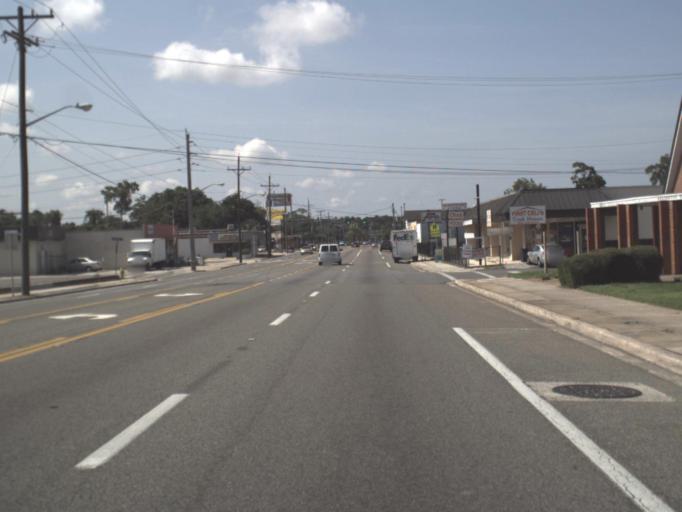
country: US
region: Florida
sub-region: Duval County
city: Jacksonville
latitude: 30.3355
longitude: -81.6028
